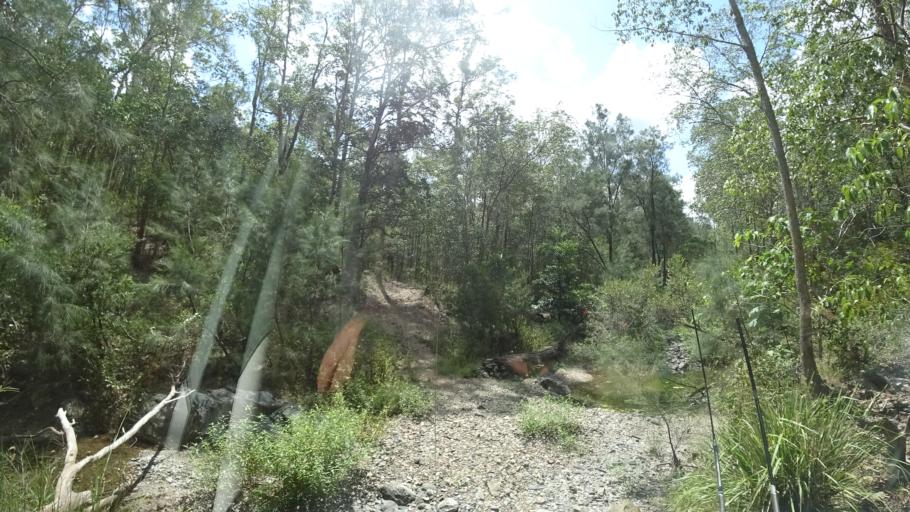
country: AU
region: Queensland
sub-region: Moreton Bay
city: Highvale
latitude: -27.3710
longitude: 152.7348
